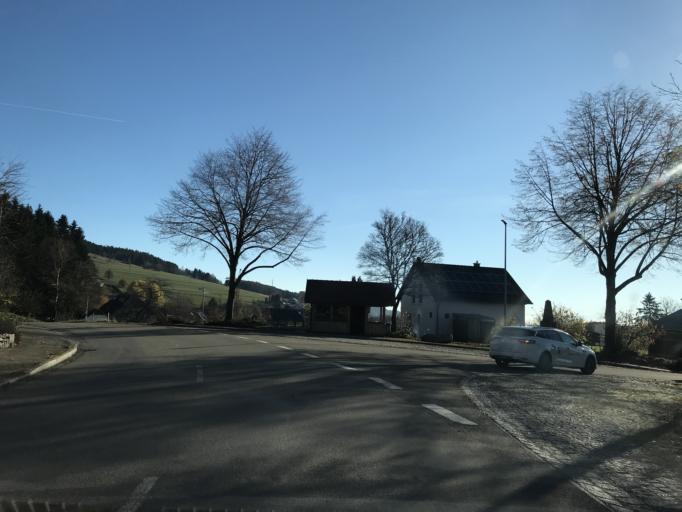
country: DE
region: Baden-Wuerttemberg
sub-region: Freiburg Region
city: Rickenbach
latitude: 47.6369
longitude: 7.9754
